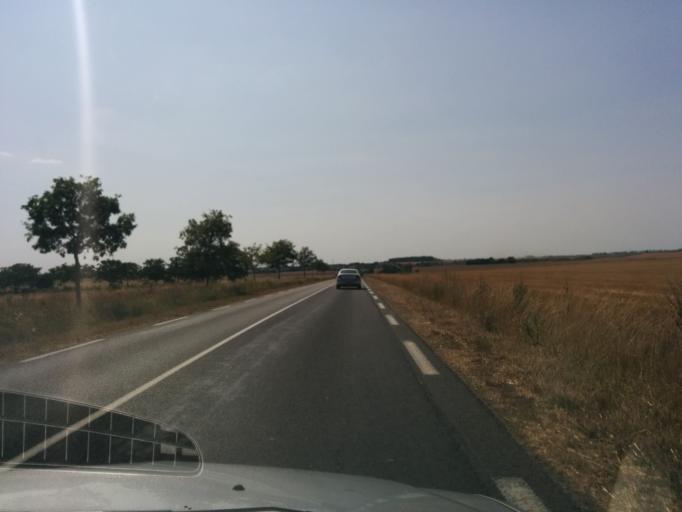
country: FR
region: Poitou-Charentes
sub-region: Departement de la Vienne
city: Avanton
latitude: 46.6867
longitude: 0.2923
